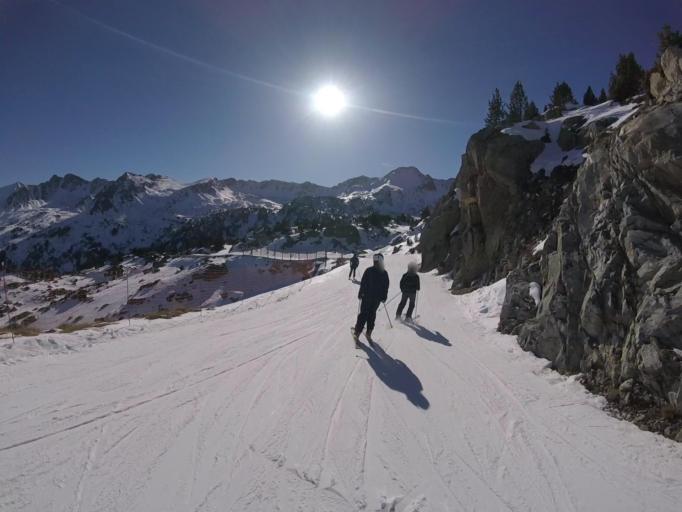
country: AD
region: Encamp
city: Pas de la Casa
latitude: 42.5298
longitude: 1.6853
